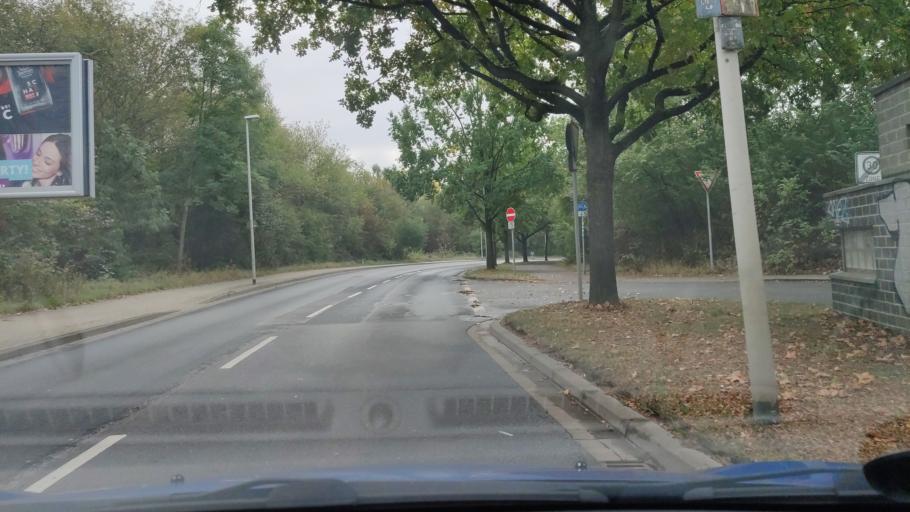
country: DE
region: Lower Saxony
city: Ronnenberg
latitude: 52.3503
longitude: 9.6749
